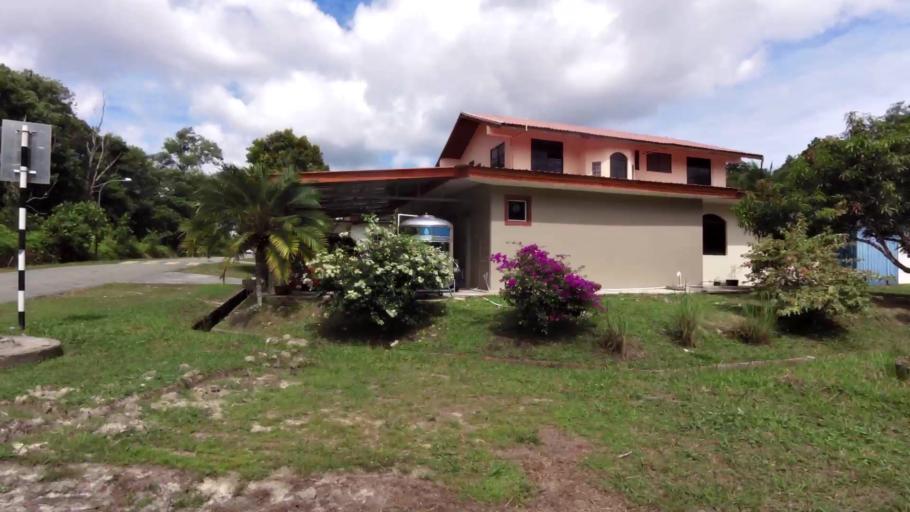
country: BN
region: Brunei and Muara
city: Bandar Seri Begawan
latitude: 4.9369
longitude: 114.9036
